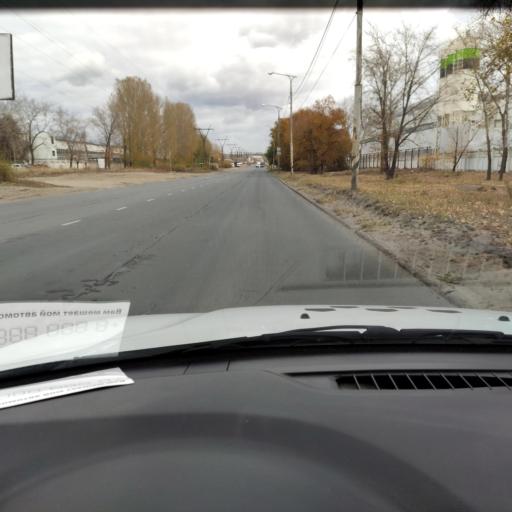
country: RU
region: Samara
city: Zhigulevsk
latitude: 53.4801
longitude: 49.4949
